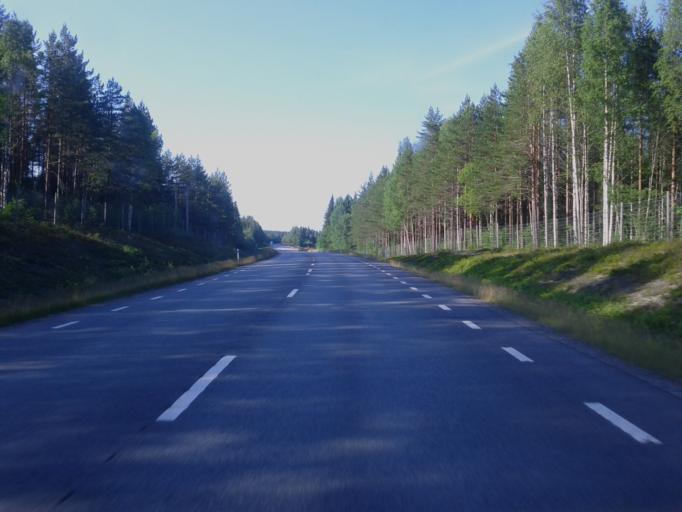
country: SE
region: Vaesterbotten
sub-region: Robertsfors Kommun
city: Robertsfors
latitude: 64.0247
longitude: 20.8413
